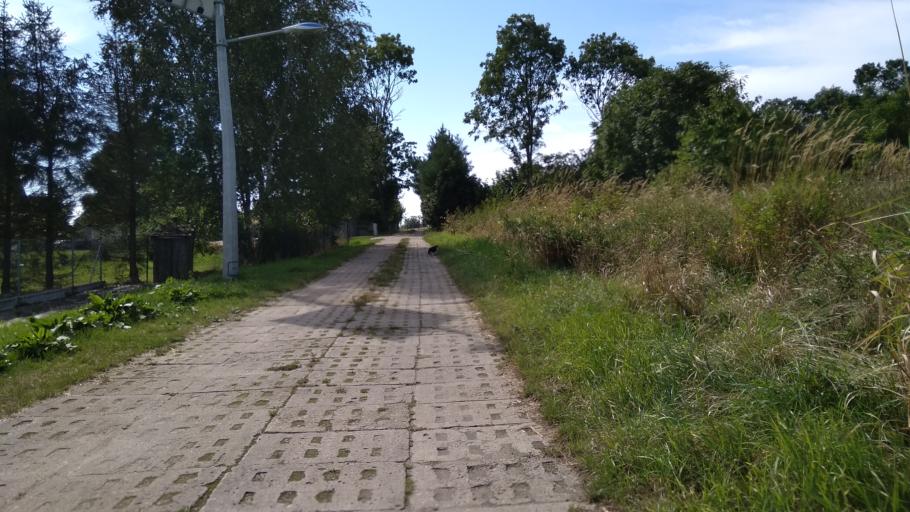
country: PL
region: West Pomeranian Voivodeship
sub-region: Powiat slawienski
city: Darlowo
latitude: 54.5113
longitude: 16.5161
